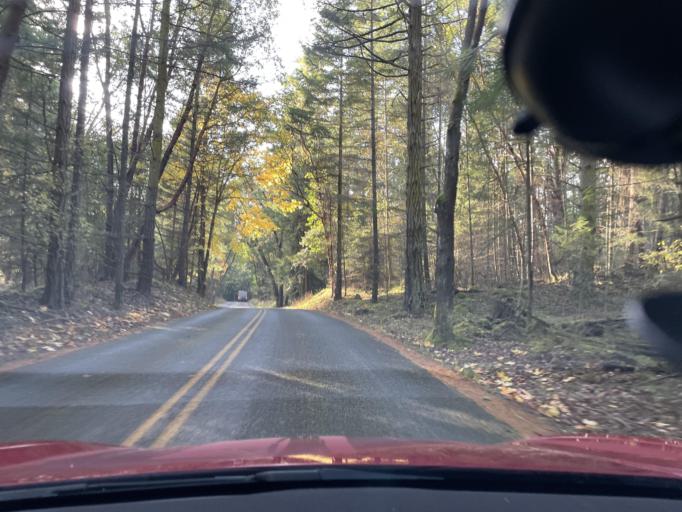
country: US
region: Washington
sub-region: San Juan County
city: Friday Harbor
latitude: 48.5211
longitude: -123.1444
